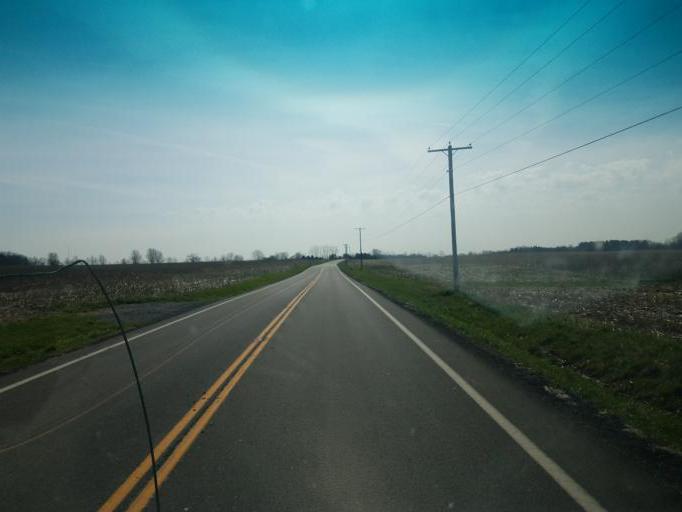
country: US
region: Ohio
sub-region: Richland County
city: Lincoln Heights
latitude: 40.8923
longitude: -82.4710
